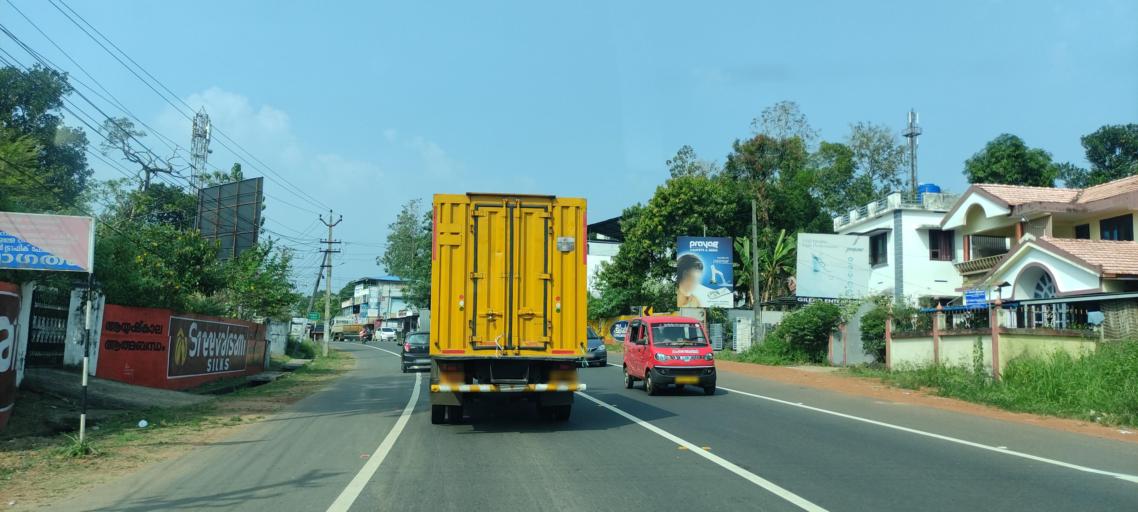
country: IN
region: Kerala
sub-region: Alappuzha
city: Chengannur
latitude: 9.2688
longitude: 76.6559
